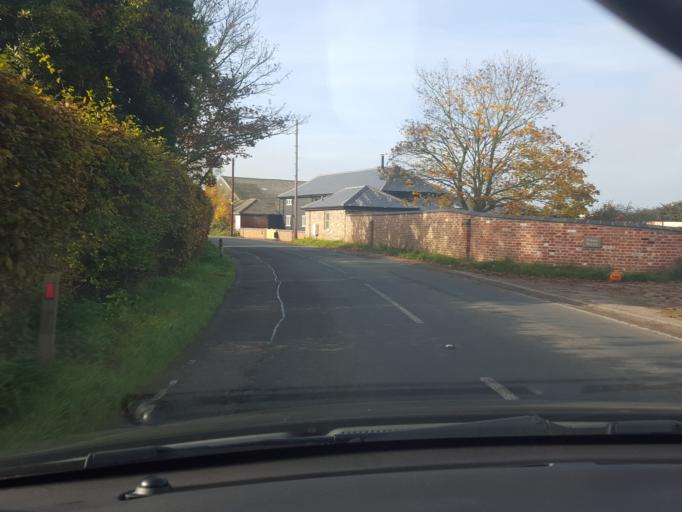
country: GB
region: England
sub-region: Essex
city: Mistley
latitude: 51.9319
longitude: 1.1577
